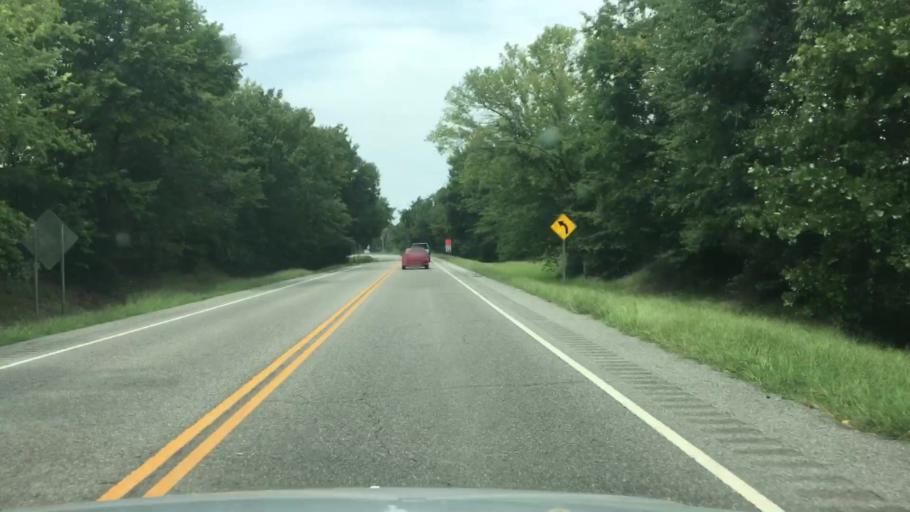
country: US
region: Oklahoma
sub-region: Muskogee County
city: Fort Gibson
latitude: 35.9355
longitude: -95.1607
